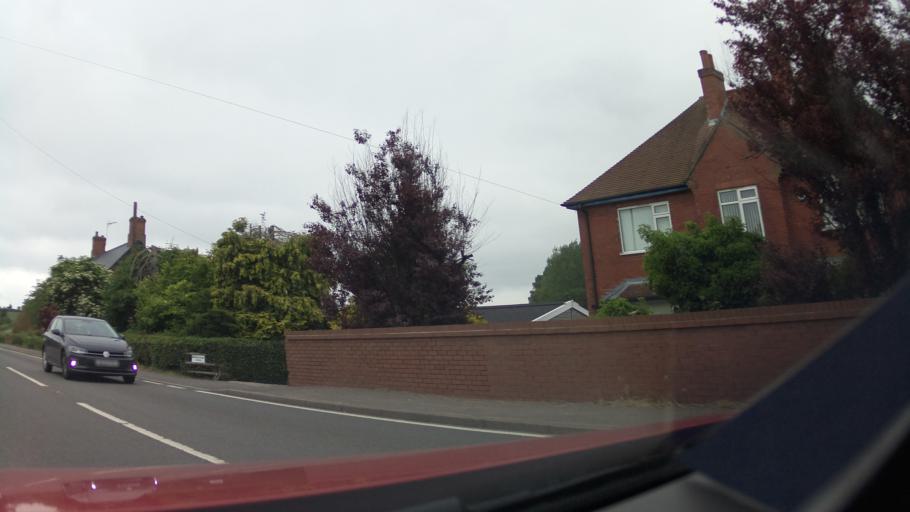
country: GB
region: England
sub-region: Derbyshire
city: Etwall
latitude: 52.9520
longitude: -1.5804
